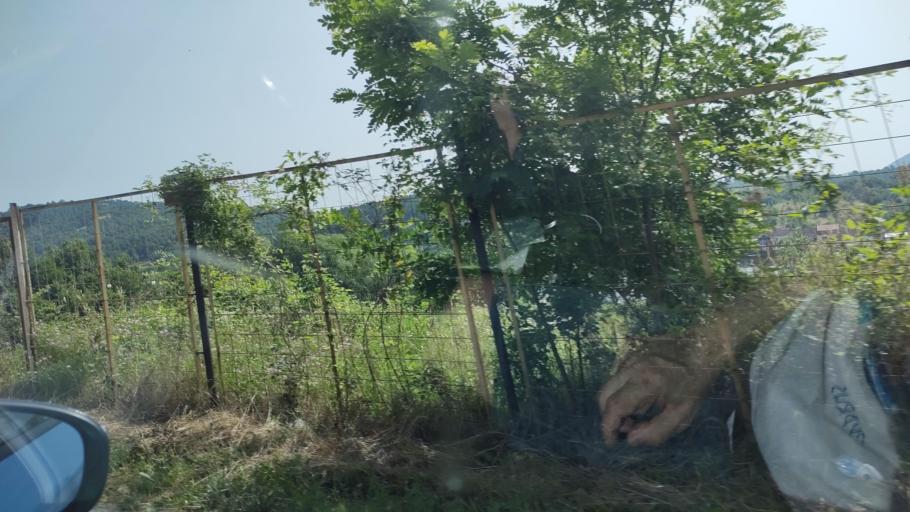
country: RO
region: Mehedinti
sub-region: Comuna Eselnita
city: Eselnita
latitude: 44.6896
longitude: 22.3634
